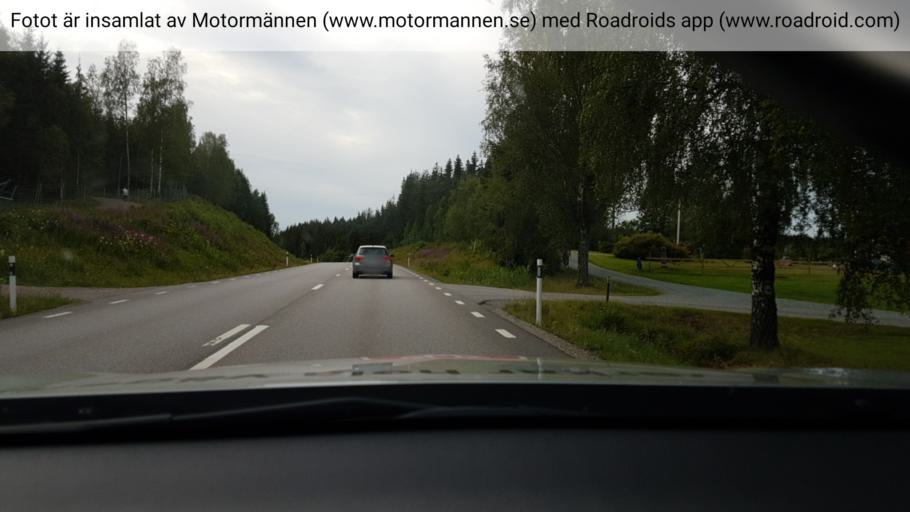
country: SE
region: Vaestra Goetaland
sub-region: Bengtsfors Kommun
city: Billingsfors
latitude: 59.0259
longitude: 12.3579
